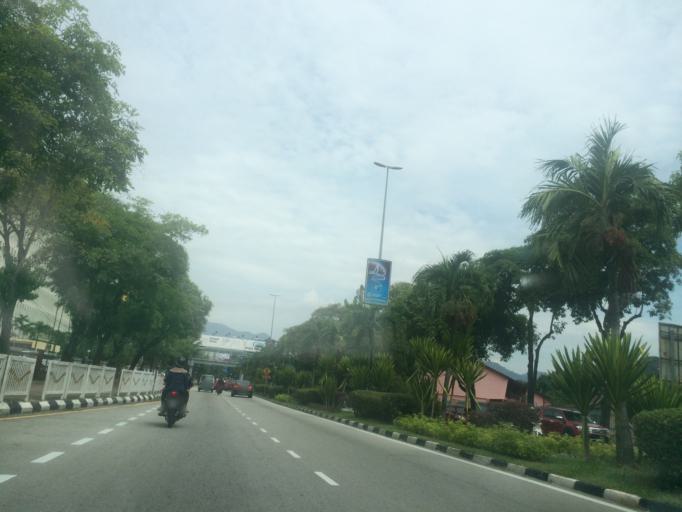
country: MY
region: Perak
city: Ipoh
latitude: 4.6045
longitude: 101.0917
